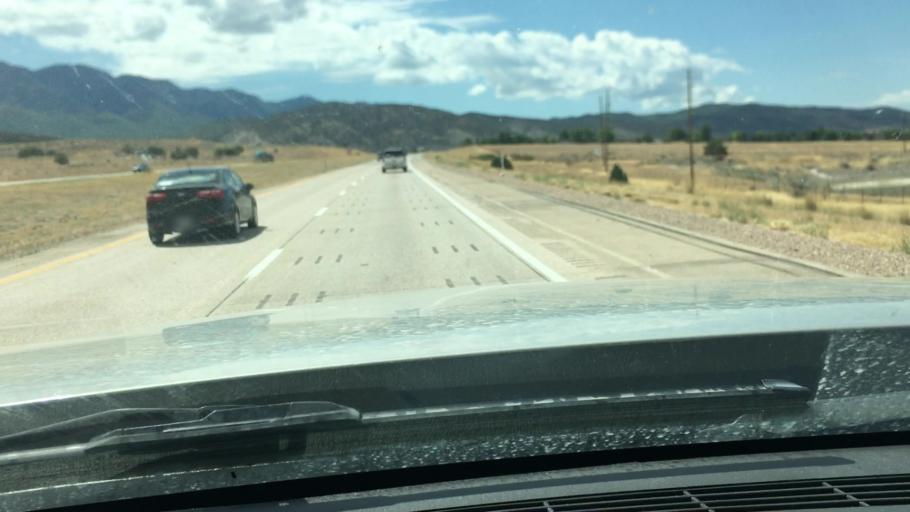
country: US
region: Utah
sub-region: Juab County
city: Nephi
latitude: 39.7375
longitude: -111.8279
